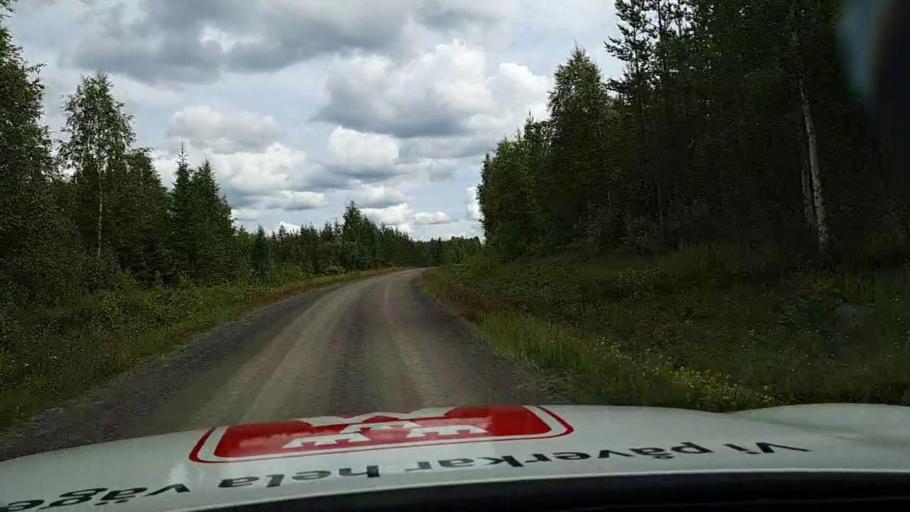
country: SE
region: Jaemtland
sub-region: OEstersunds Kommun
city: Lit
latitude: 63.3006
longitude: 15.3139
